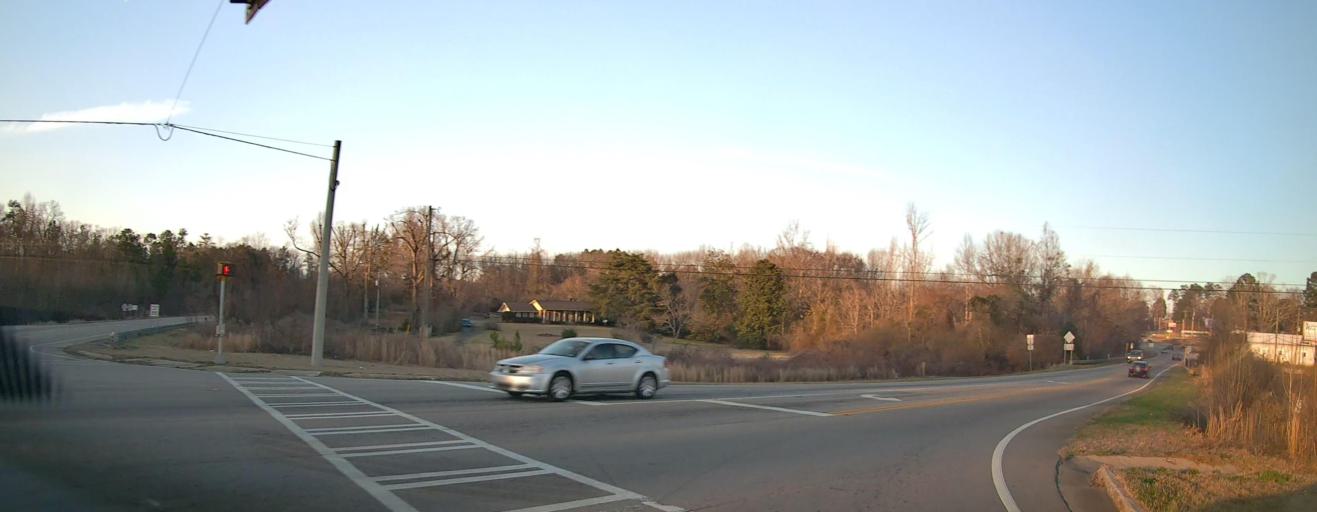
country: US
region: Georgia
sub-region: Troup County
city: La Grange
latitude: 33.0181
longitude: -85.0876
